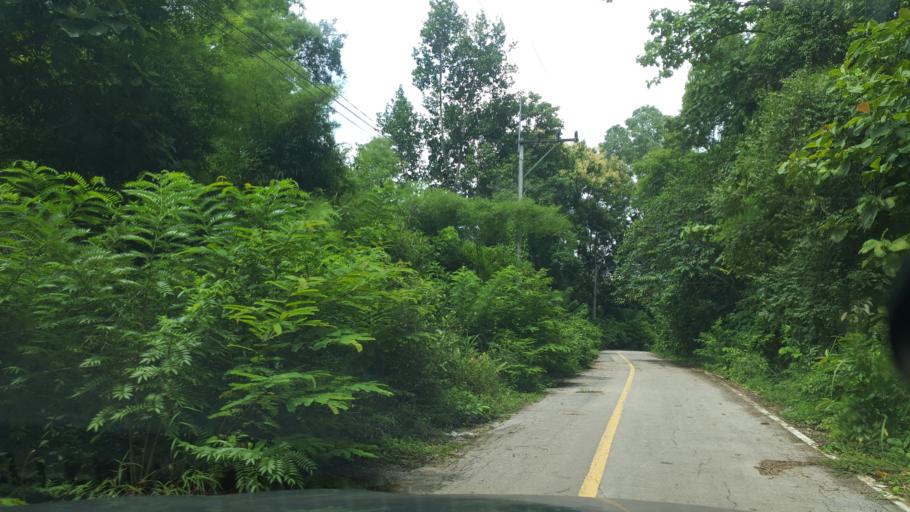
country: TH
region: Lampang
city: Hang Chat
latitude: 18.3554
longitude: 99.2542
